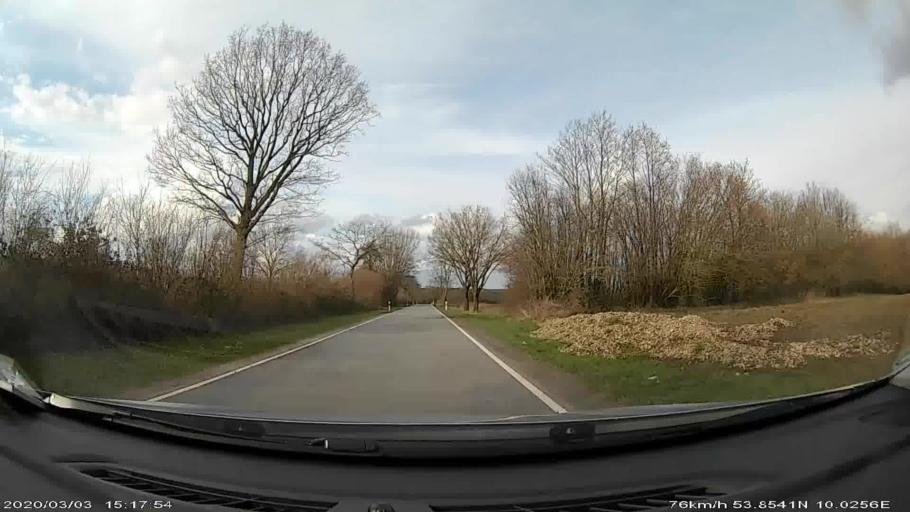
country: DE
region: Schleswig-Holstein
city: Kattendorf
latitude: 53.8535
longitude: 10.0255
